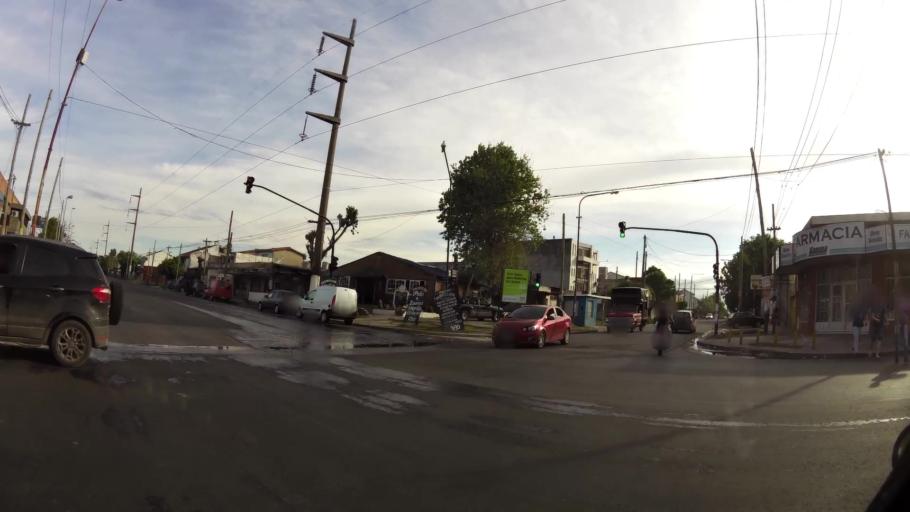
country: AR
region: Buenos Aires
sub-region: Partido de Quilmes
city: Quilmes
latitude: -34.7436
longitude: -58.2728
